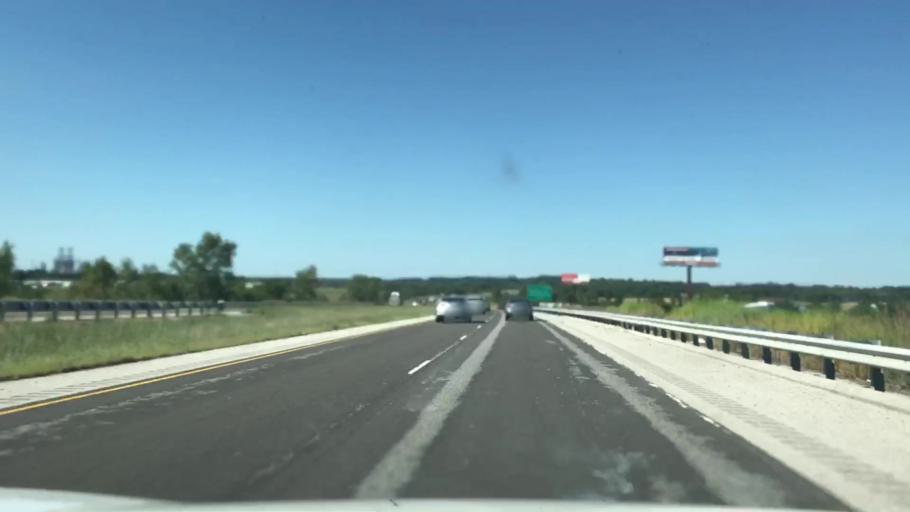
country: US
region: Illinois
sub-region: Madison County
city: South Roxana
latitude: 38.8181
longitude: -90.0420
